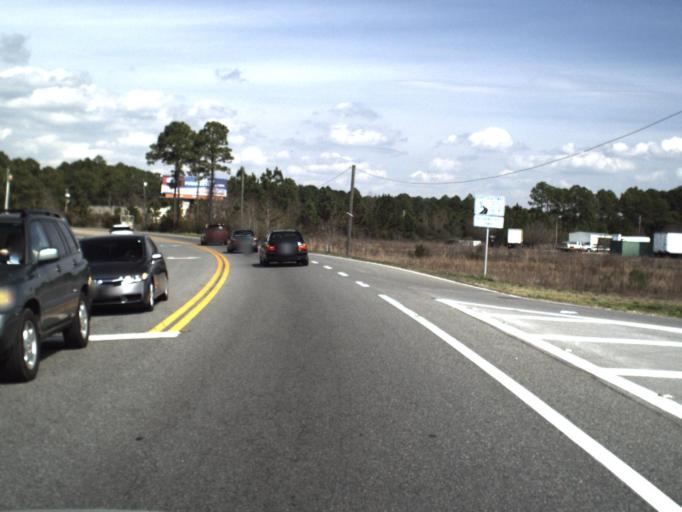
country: US
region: Florida
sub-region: Bay County
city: Pretty Bayou
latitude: 30.2043
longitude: -85.6735
